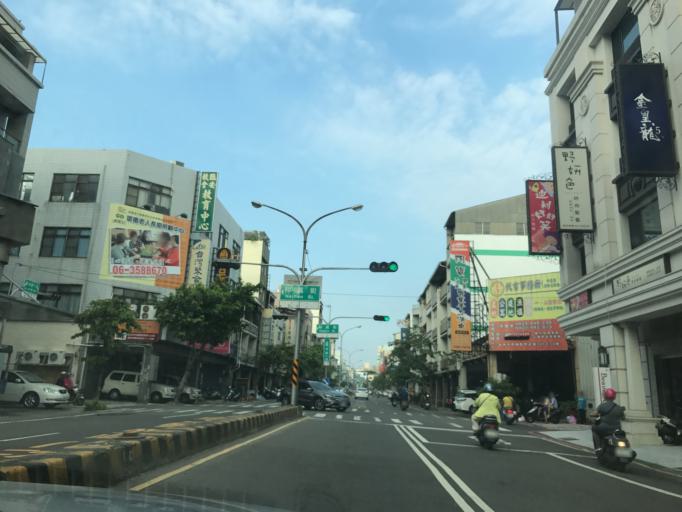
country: TW
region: Taiwan
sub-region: Tainan
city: Tainan
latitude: 22.9991
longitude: 120.1906
